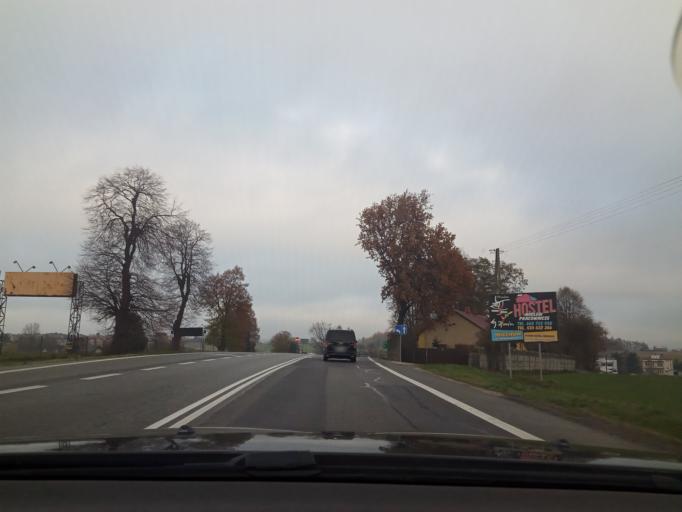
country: PL
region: Lesser Poland Voivodeship
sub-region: Powiat miechowski
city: Miechow
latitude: 50.3436
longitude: 20.0350
